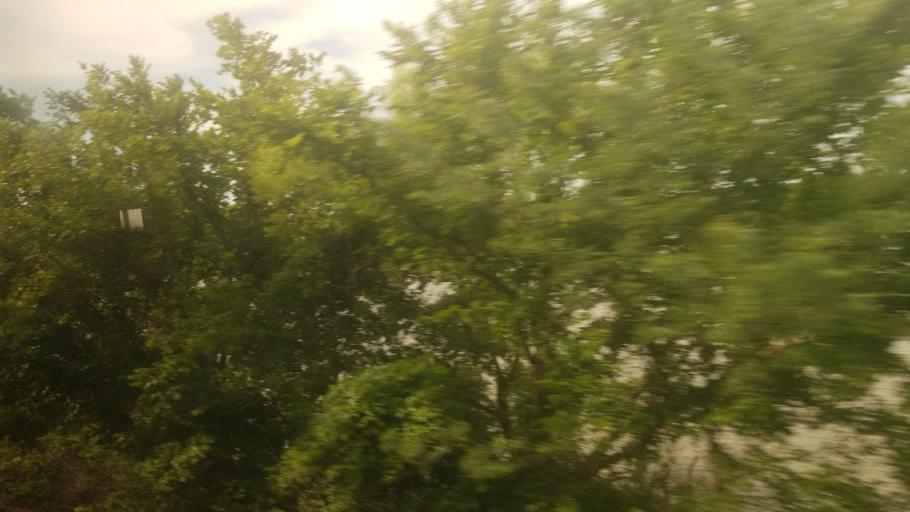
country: US
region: Kansas
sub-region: Douglas County
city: Lawrence
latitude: 39.0225
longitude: -95.3096
